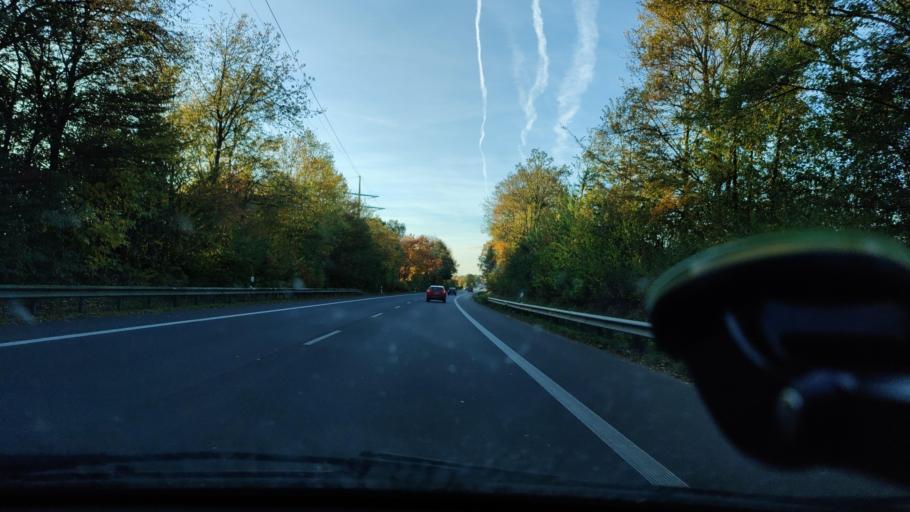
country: DE
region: North Rhine-Westphalia
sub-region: Regierungsbezirk Dusseldorf
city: Monchengladbach
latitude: 51.2292
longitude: 6.4663
